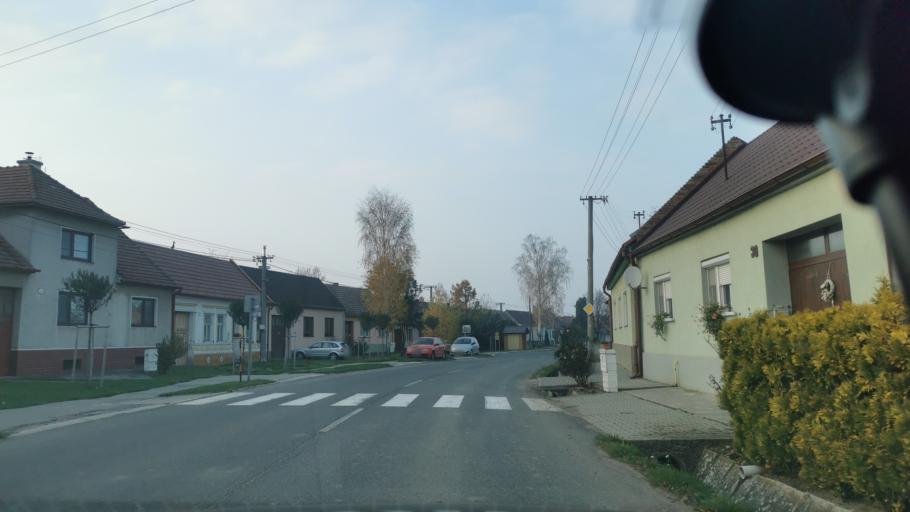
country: SK
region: Trnavsky
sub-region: Okres Skalica
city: Holic
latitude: 48.8048
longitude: 17.1954
